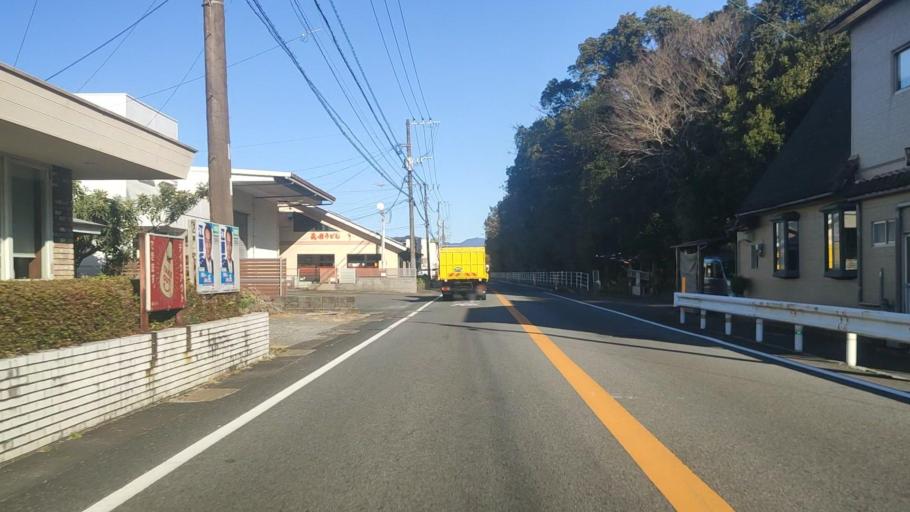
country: JP
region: Miyazaki
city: Nobeoka
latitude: 32.5261
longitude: 131.6825
